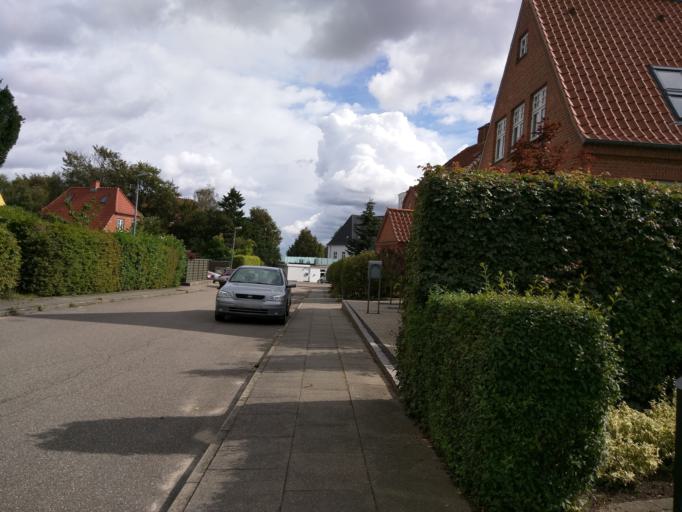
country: DK
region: Central Jutland
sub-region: Viborg Kommune
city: Viborg
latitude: 56.4592
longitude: 9.4071
